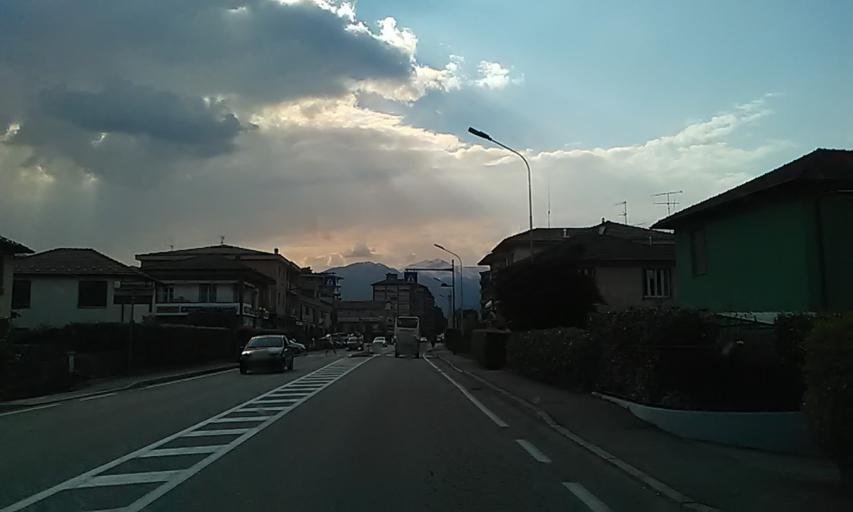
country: IT
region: Piedmont
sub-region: Provincia Verbano-Cusio-Ossola
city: Verbania
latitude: 45.9280
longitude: 8.5580
